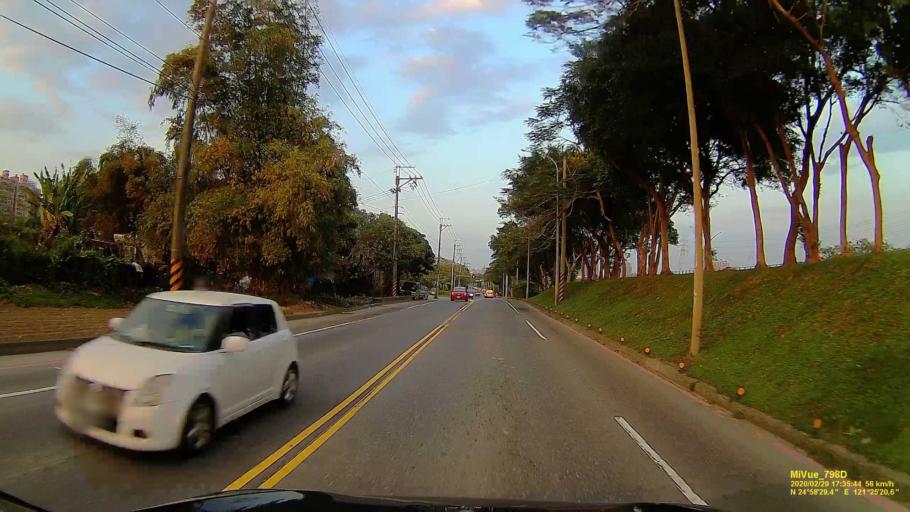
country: TW
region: Taipei
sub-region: Taipei
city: Banqiao
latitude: 24.9749
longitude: 121.4226
